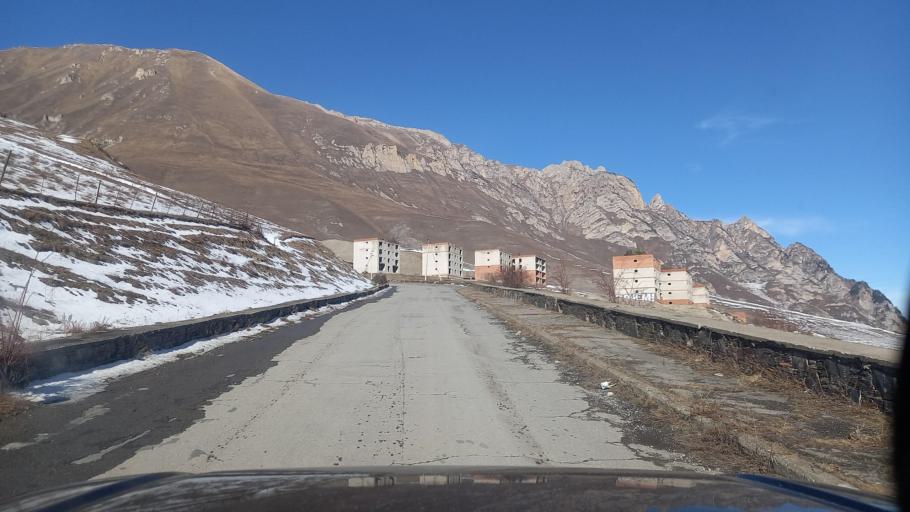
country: RU
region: Ingushetiya
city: Dzhayrakh
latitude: 42.8424
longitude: 44.5116
